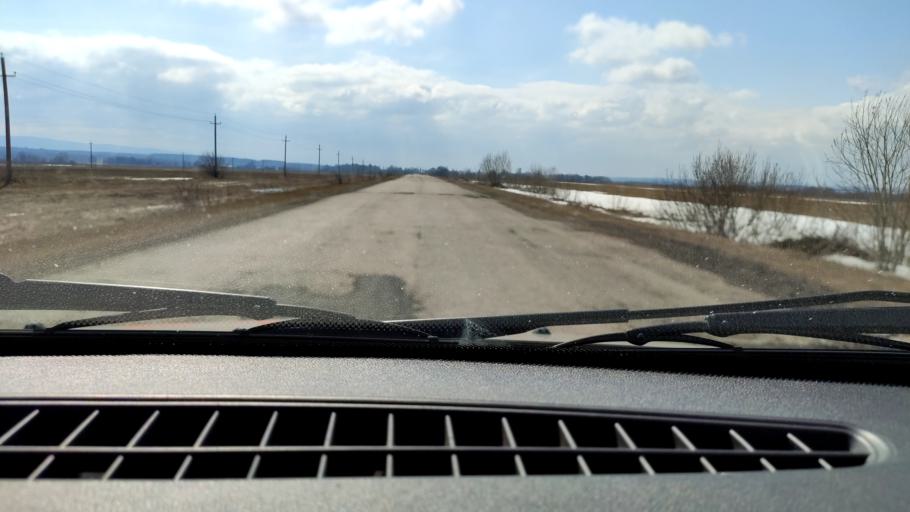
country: RU
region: Bashkortostan
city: Kudeyevskiy
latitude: 54.8423
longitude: 56.7956
